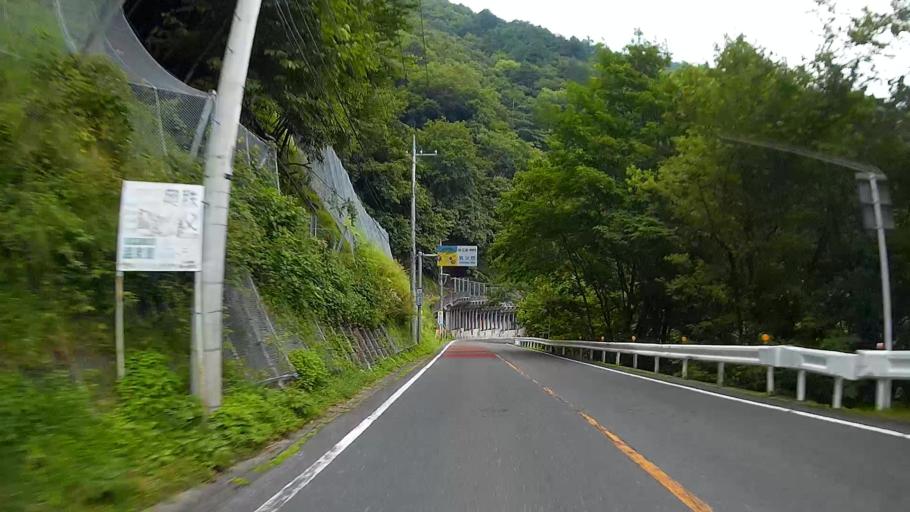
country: JP
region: Yamanashi
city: Enzan
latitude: 35.9127
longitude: 138.8206
